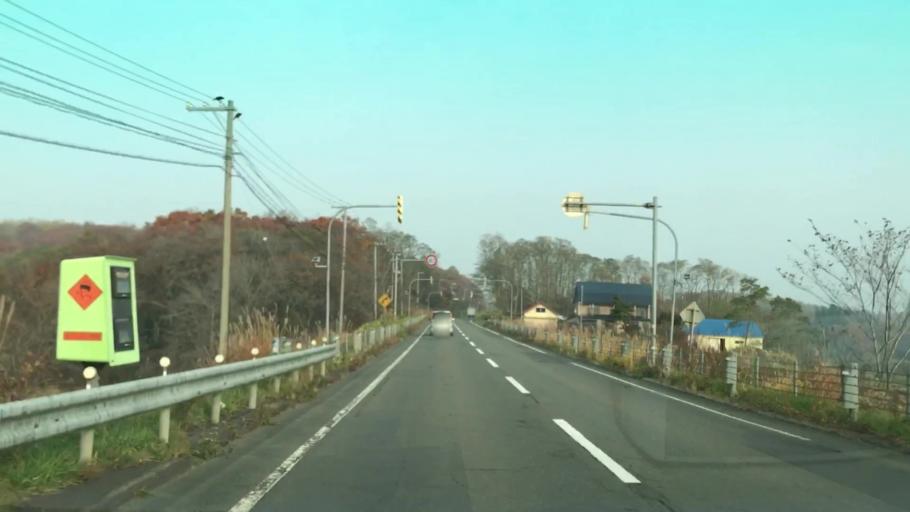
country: JP
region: Hokkaido
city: Ishikari
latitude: 43.3251
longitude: 141.4432
